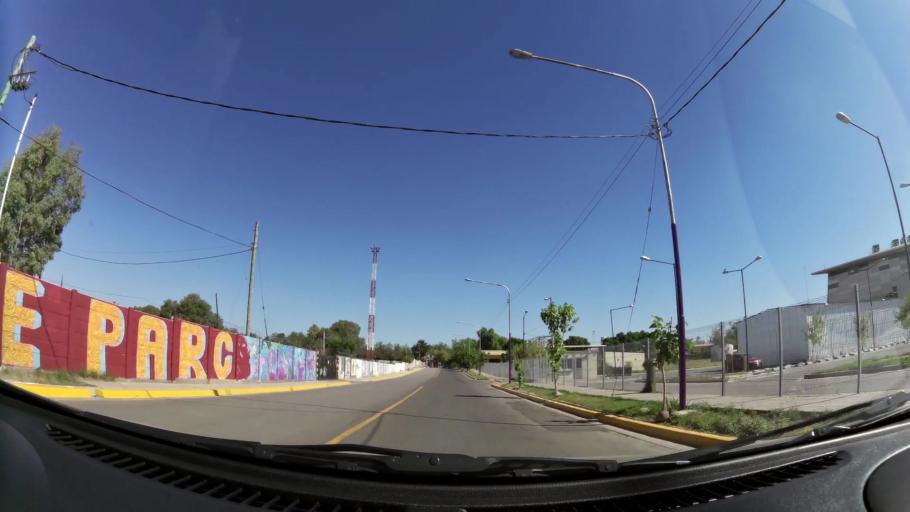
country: AR
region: Mendoza
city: Mendoza
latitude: -32.8874
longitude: -68.8127
